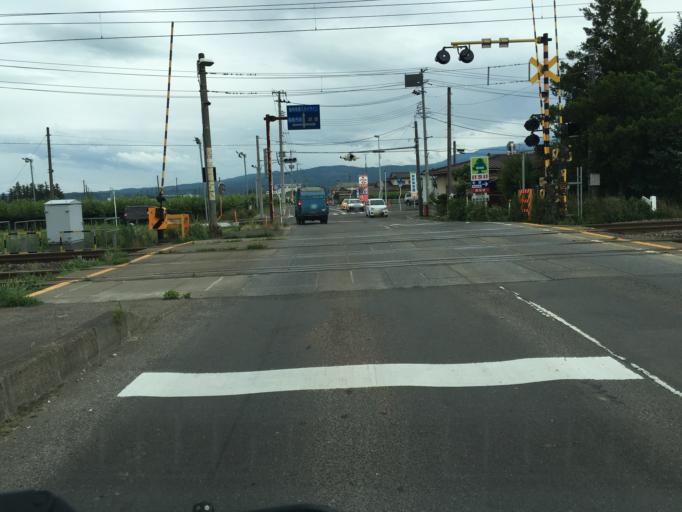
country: JP
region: Fukushima
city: Fukushima-shi
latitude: 37.7698
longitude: 140.4022
